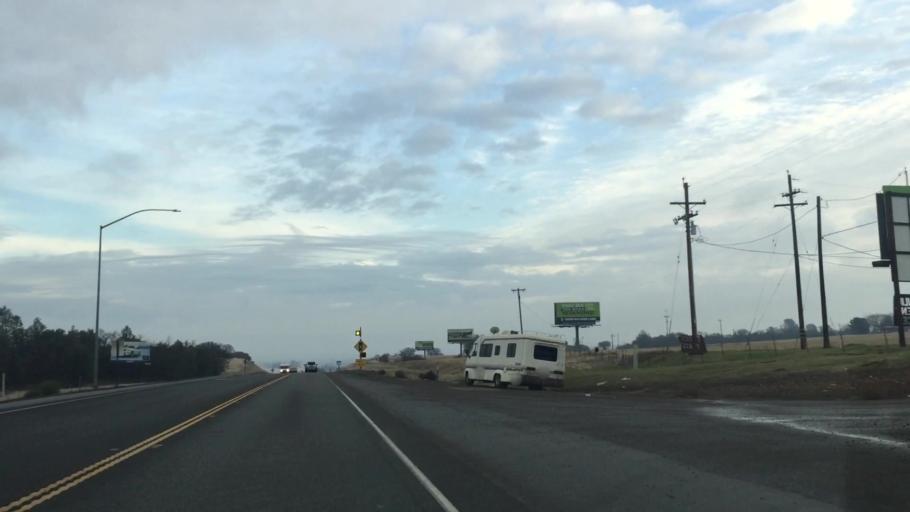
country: US
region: California
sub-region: Butte County
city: South Oroville
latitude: 39.4584
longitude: -121.5842
